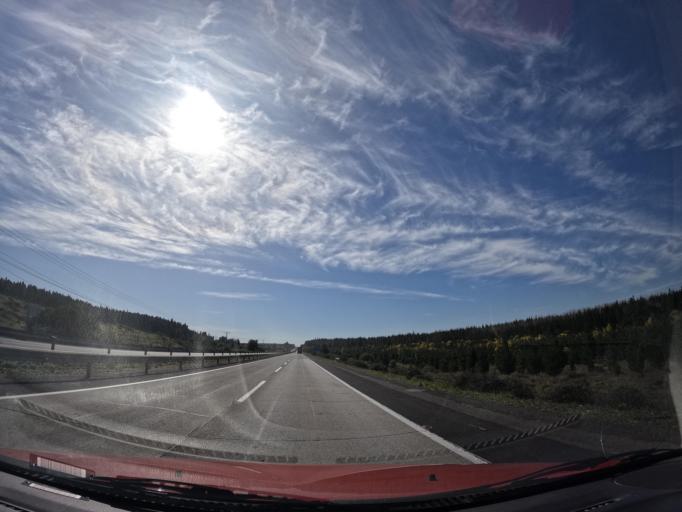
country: CL
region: Biobio
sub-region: Provincia de Biobio
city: Cabrero
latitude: -36.9504
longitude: -72.3524
